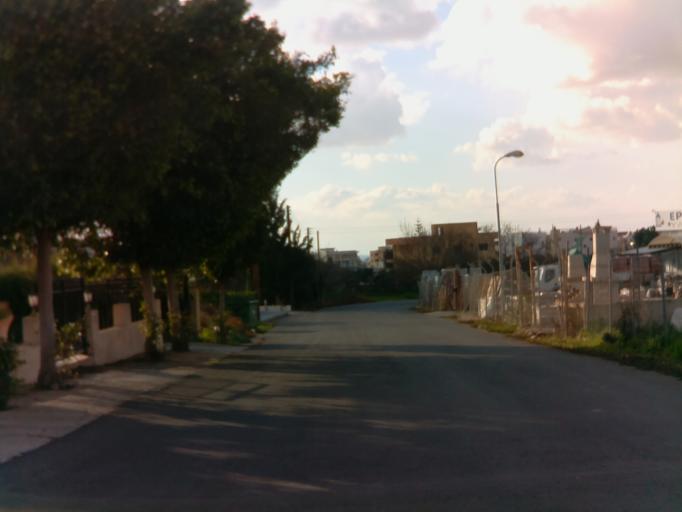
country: CY
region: Pafos
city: Chlorakas
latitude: 34.7996
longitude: 32.4206
